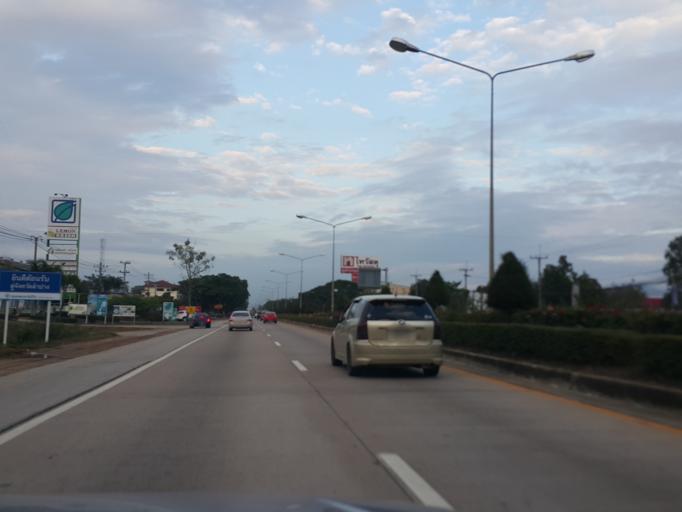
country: TH
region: Lampang
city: Lampang
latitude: 18.2677
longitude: 99.4718
